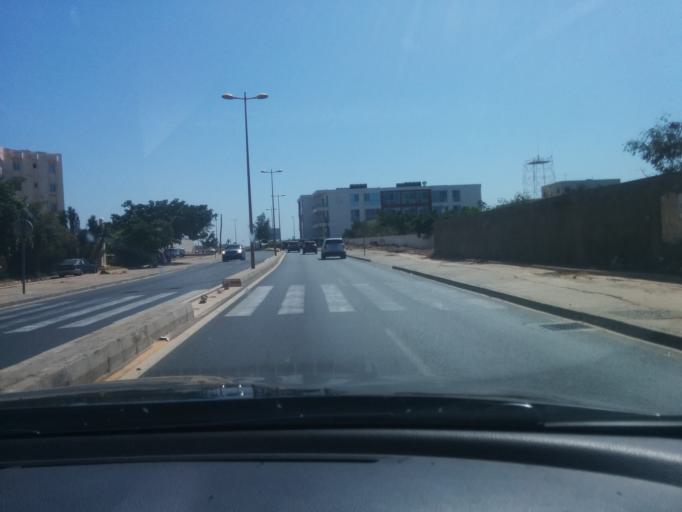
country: SN
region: Dakar
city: Mermoz Boabab
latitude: 14.7061
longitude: -17.4833
